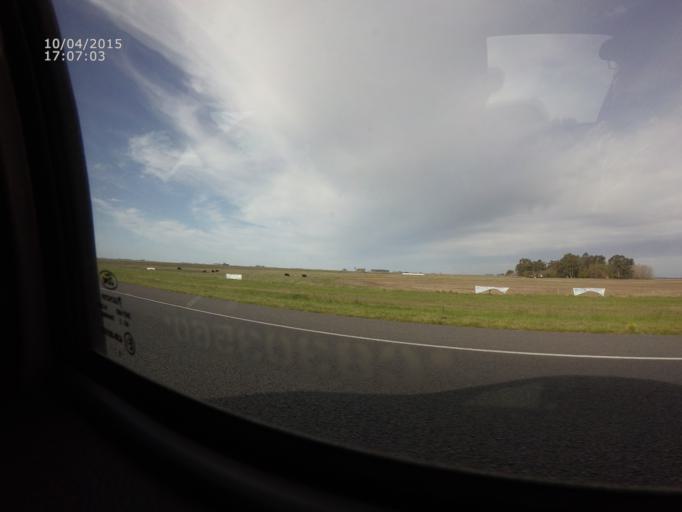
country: AR
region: Buenos Aires
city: Coronel Vidal
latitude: -37.3558
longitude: -57.7553
